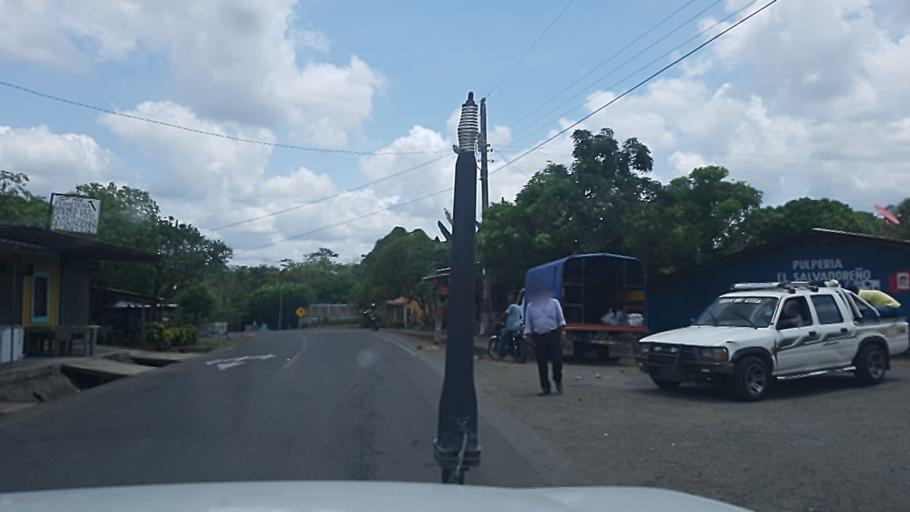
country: NI
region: Atlantico Sur
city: Muelle de los Bueyes
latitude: 11.9208
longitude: -84.6495
